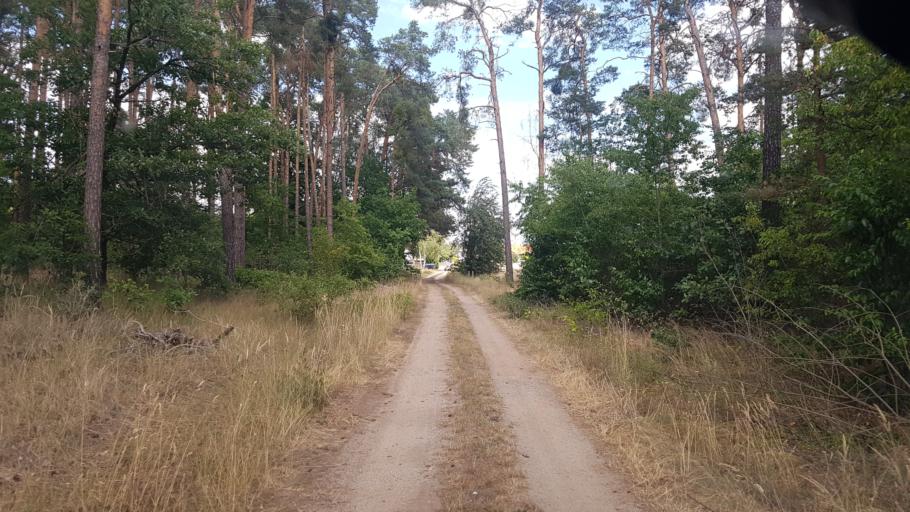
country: DE
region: Brandenburg
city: Schonborn
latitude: 51.5625
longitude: 13.4783
